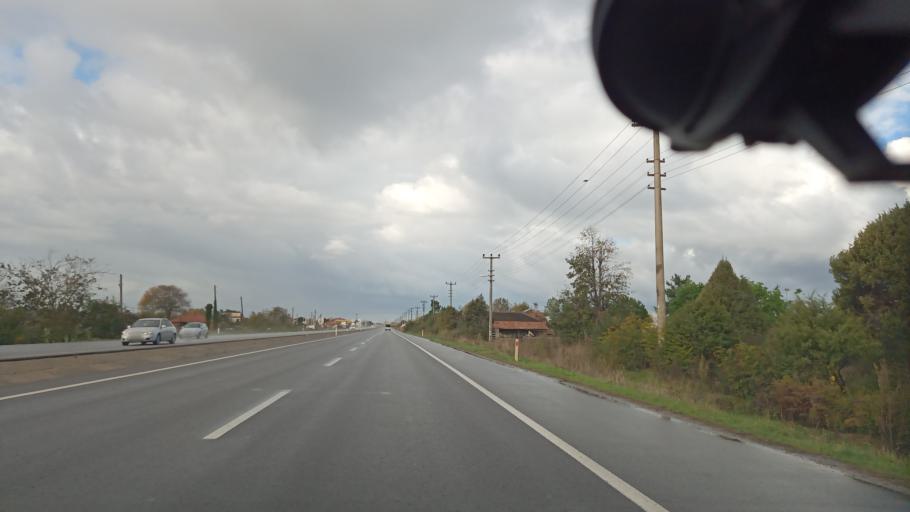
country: TR
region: Sakarya
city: Karasu
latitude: 41.0783
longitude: 30.7758
